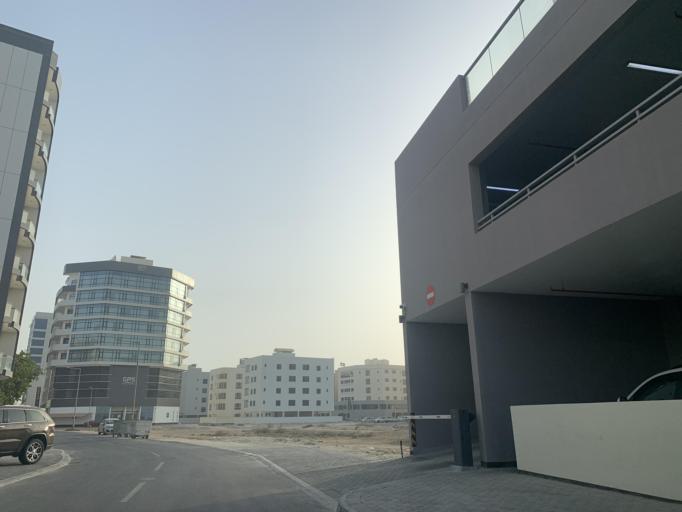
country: BH
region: Manama
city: Jidd Hafs
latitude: 26.2417
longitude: 50.5325
